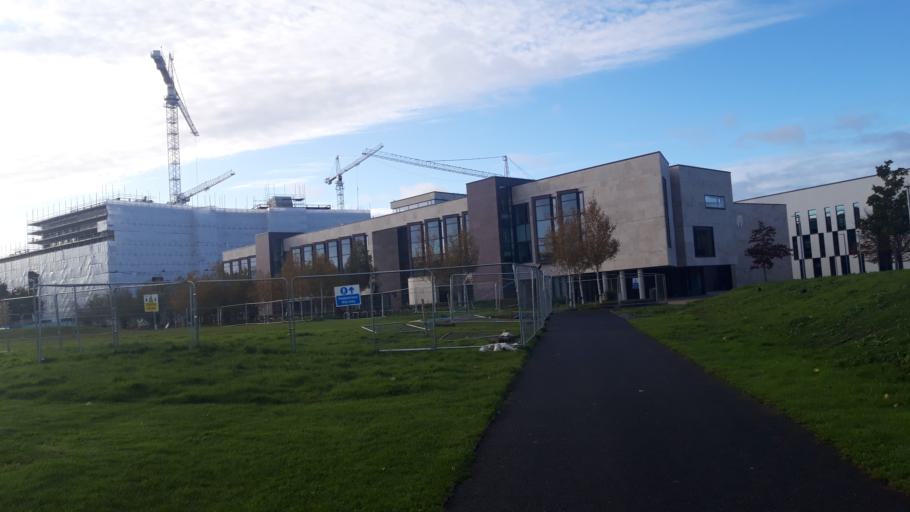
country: IE
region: Leinster
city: Mount Merrion
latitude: 53.3052
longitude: -6.2179
